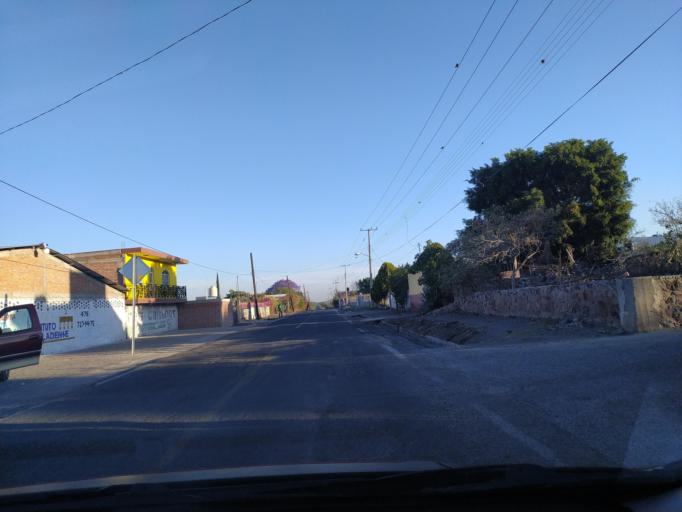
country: MX
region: Guanajuato
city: Ciudad Manuel Doblado
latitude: 20.7491
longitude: -101.8246
